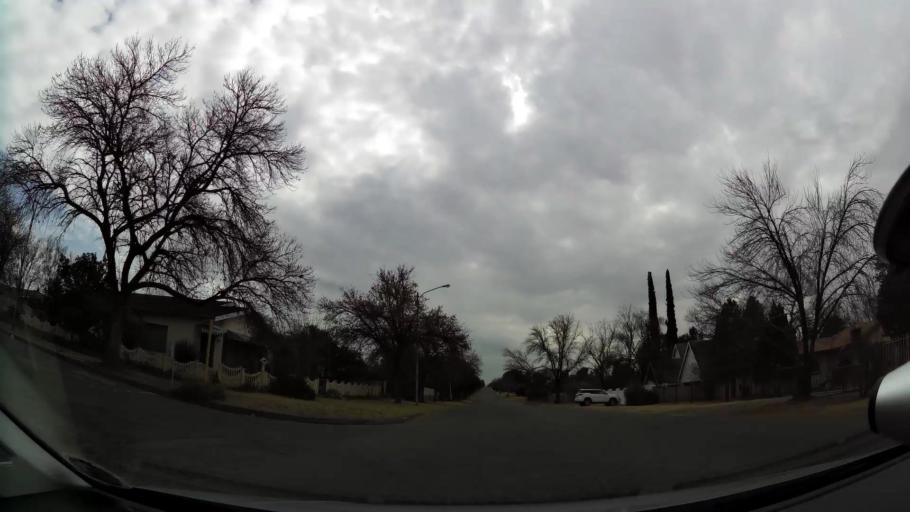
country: ZA
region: Orange Free State
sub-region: Fezile Dabi District Municipality
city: Kroonstad
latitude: -27.6466
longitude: 27.2386
